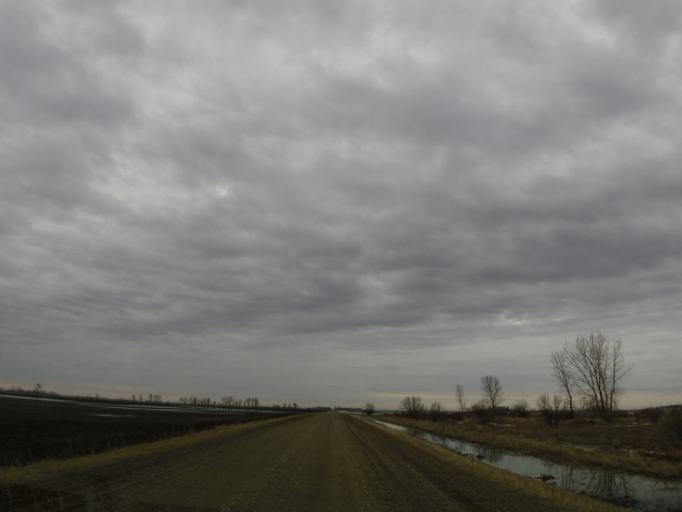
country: US
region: North Dakota
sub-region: Walsh County
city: Grafton
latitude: 48.4088
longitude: -97.4485
